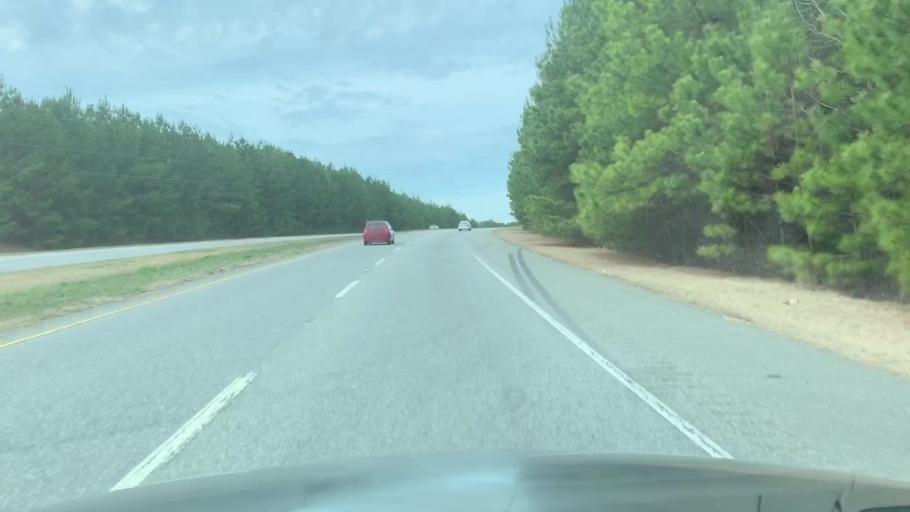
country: US
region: South Carolina
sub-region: Greenville County
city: Golden Grove
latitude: 34.7329
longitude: -82.4255
